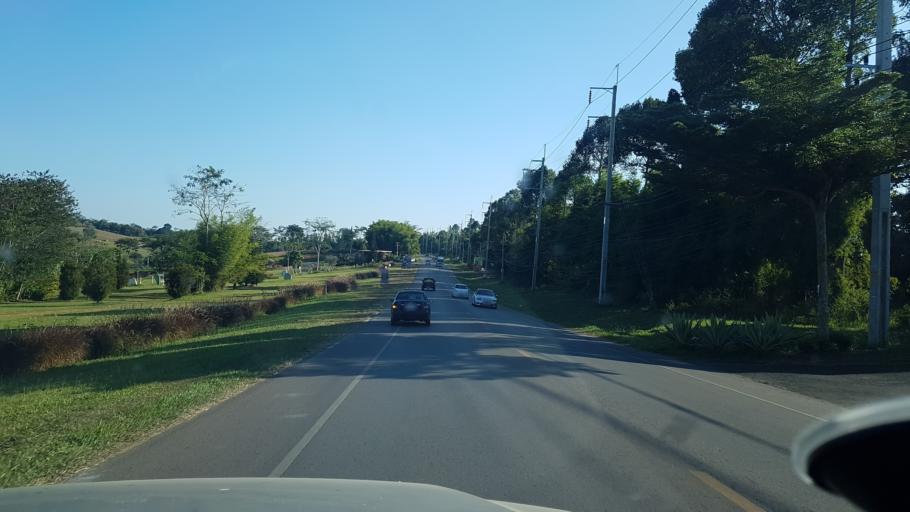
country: TH
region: Phetchabun
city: Khao Kho
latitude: 16.7456
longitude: 101.0192
